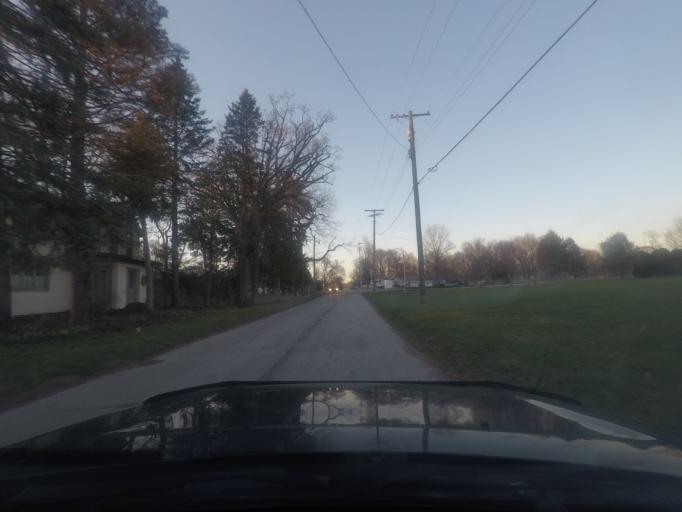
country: US
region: Indiana
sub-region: LaPorte County
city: Kingsford Heights
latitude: 41.5208
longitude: -86.7020
